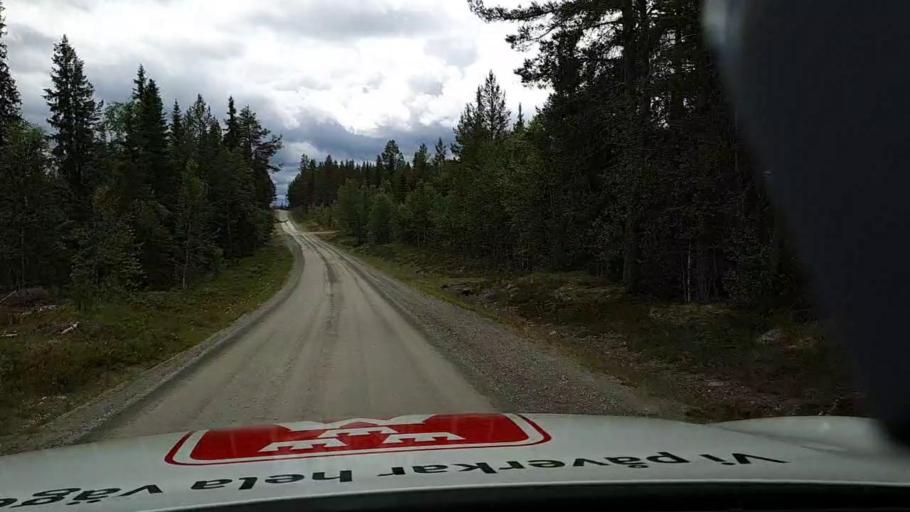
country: SE
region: Jaemtland
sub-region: Are Kommun
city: Jarpen
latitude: 62.8191
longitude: 13.8091
